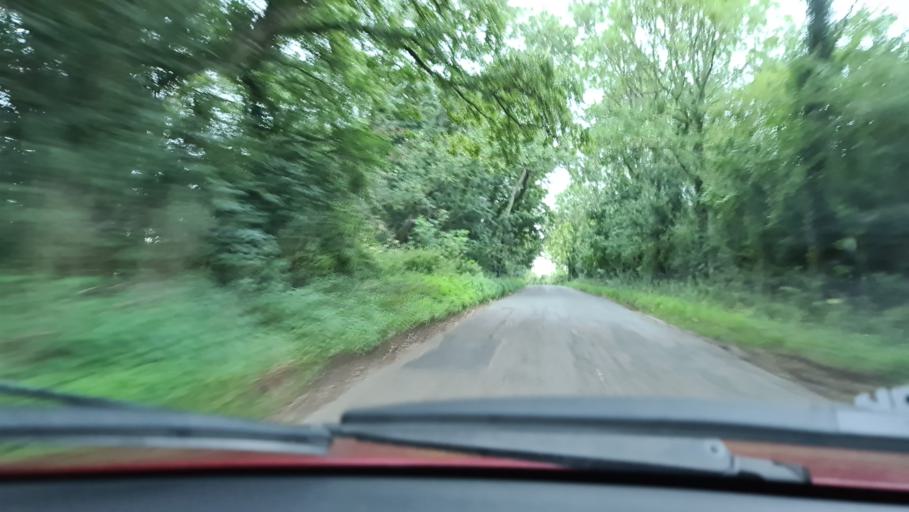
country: GB
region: England
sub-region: Oxfordshire
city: Somerton
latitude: 51.9588
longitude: -1.2993
